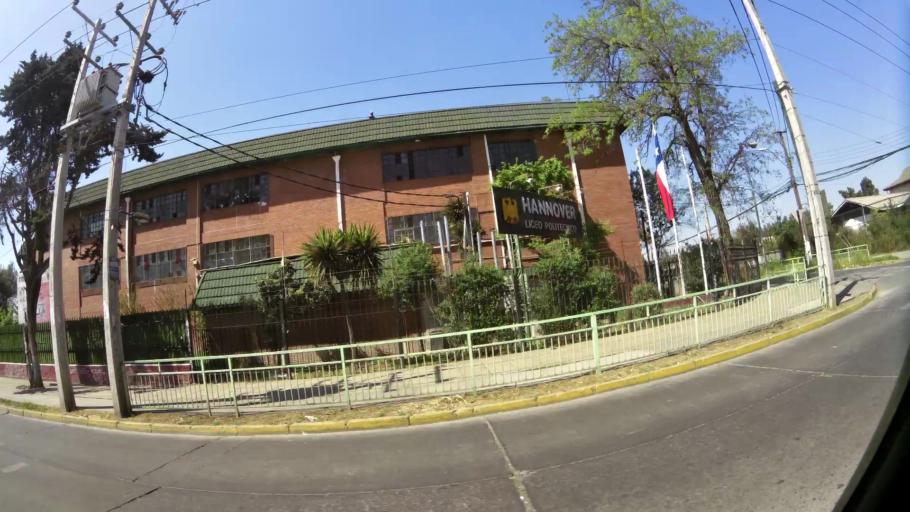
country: CL
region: Santiago Metropolitan
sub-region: Provincia de Santiago
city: Lo Prado
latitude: -33.4993
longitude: -70.7448
